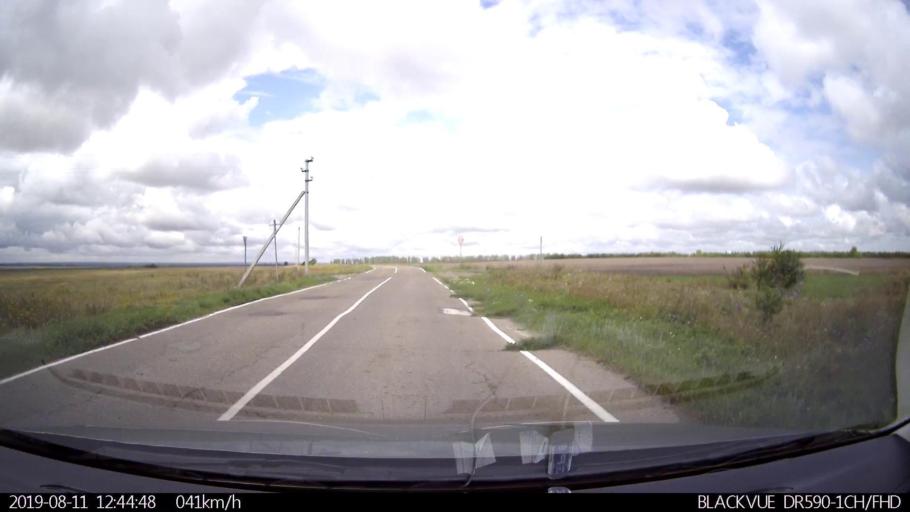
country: RU
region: Ulyanovsk
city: Ignatovka
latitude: 53.8564
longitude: 47.7332
